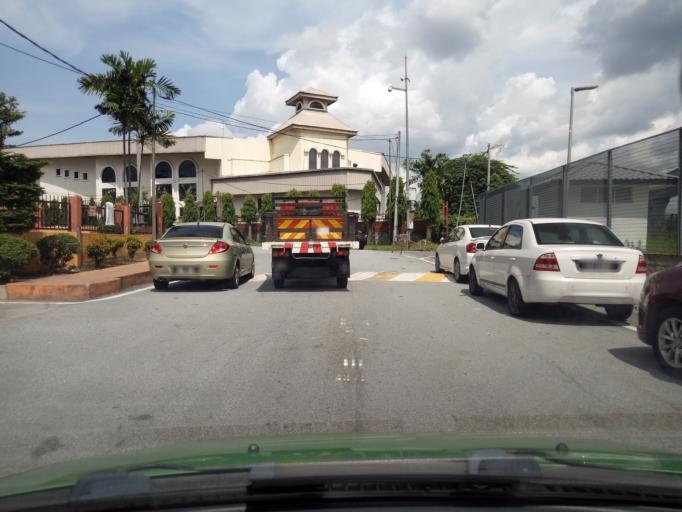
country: MY
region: Selangor
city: Kampong Baharu Balakong
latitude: 2.9890
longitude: 101.7898
